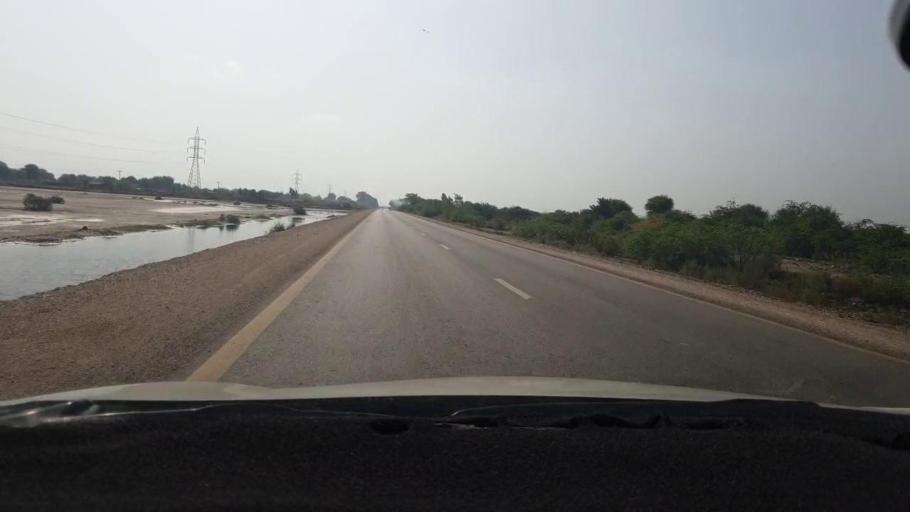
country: PK
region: Sindh
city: Jhol
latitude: 25.9088
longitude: 69.0152
